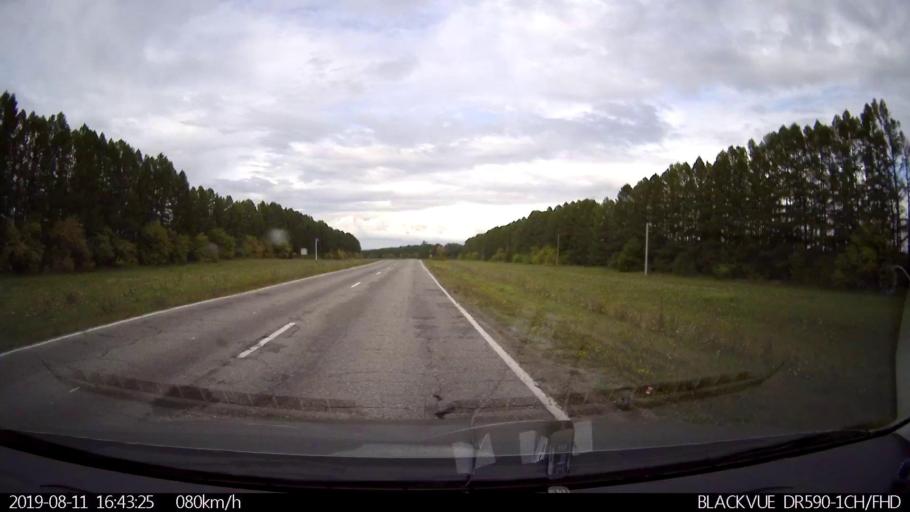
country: RU
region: Ulyanovsk
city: Mayna
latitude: 54.1689
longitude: 47.6720
